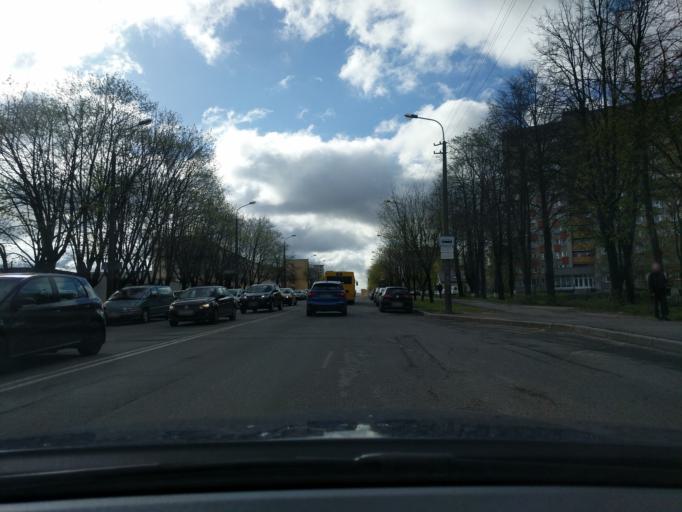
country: BY
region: Minsk
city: Novoye Medvezhino
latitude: 53.9167
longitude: 27.5027
